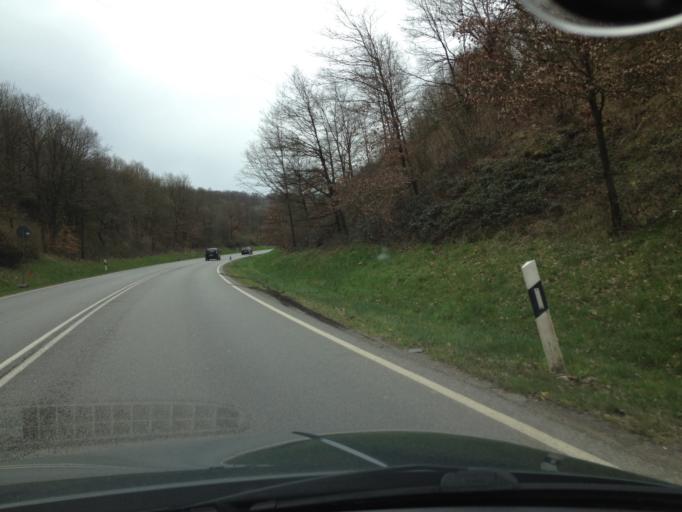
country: DE
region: Rheinland-Pfalz
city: Ehweiler
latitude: 49.5205
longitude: 7.3801
